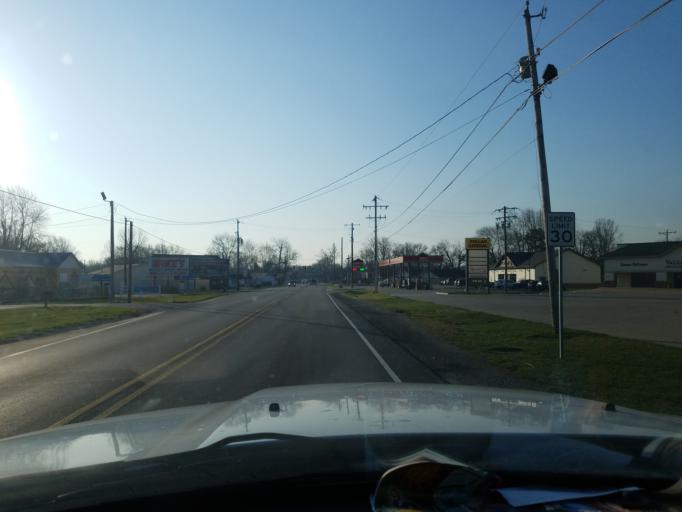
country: US
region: Indiana
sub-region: Vigo County
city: Seelyville
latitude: 39.3928
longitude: -87.3069
